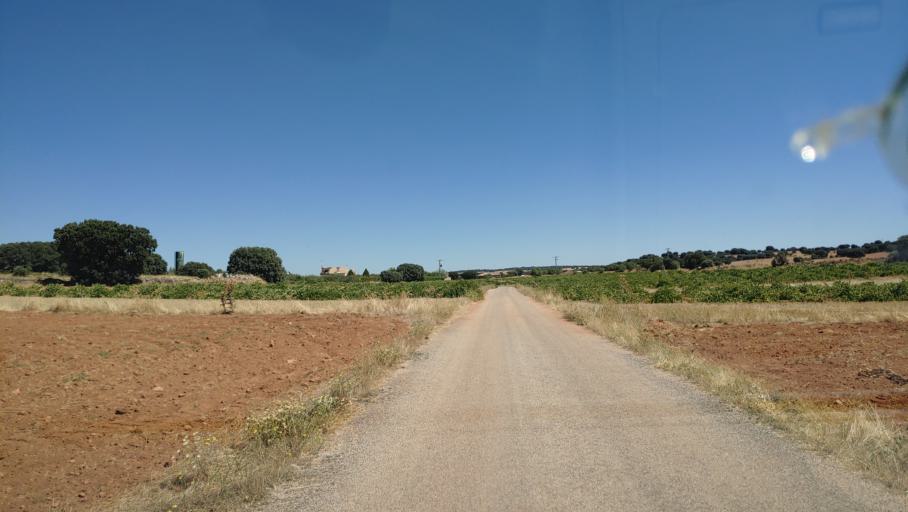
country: ES
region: Castille-La Mancha
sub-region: Provincia de Albacete
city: Ossa de Montiel
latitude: 38.9331
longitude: -2.7650
